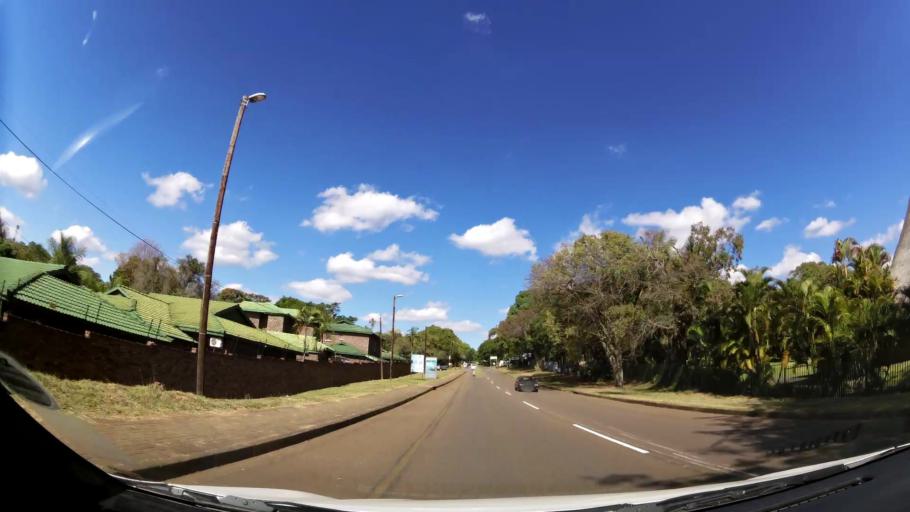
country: ZA
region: Limpopo
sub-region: Mopani District Municipality
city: Tzaneen
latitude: -23.8305
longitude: 30.1519
